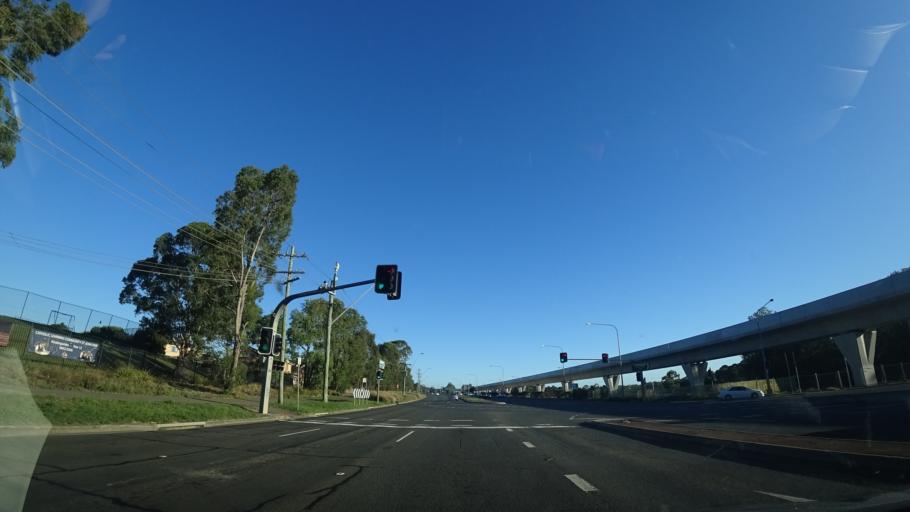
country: AU
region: New South Wales
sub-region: The Hills Shire
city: Beaumont Hills
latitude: -33.7047
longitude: 150.9304
